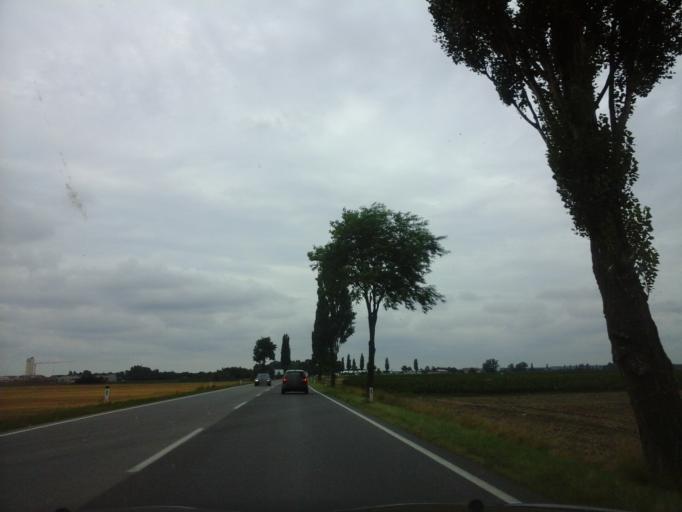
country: AT
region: Lower Austria
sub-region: Politischer Bezirk Ganserndorf
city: Engelhartstetten
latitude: 48.1695
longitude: 16.8930
